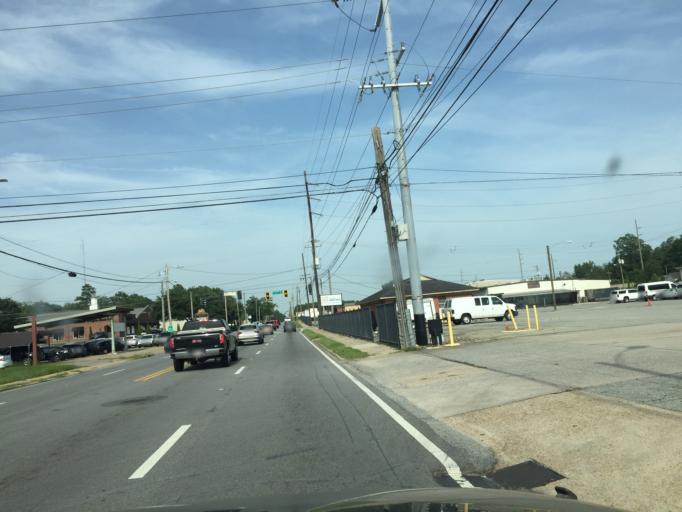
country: US
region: Georgia
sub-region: Thomas County
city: Thomasville
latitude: 30.8355
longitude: -83.9691
